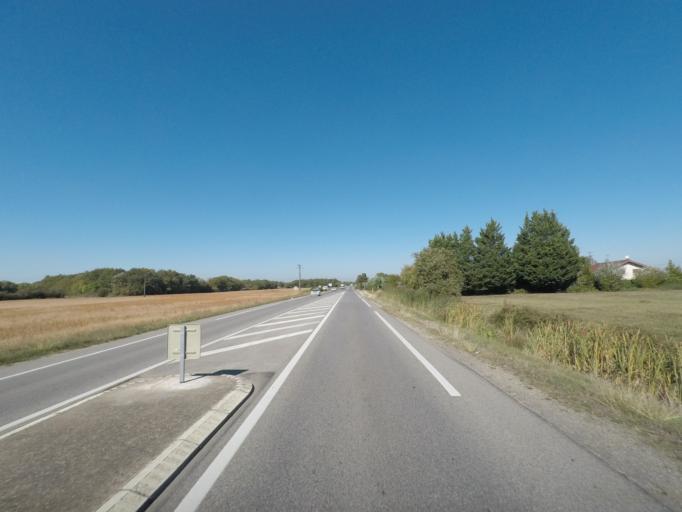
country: FR
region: Rhone-Alpes
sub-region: Departement de l'Ain
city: Viriat
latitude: 46.2533
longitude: 5.1821
